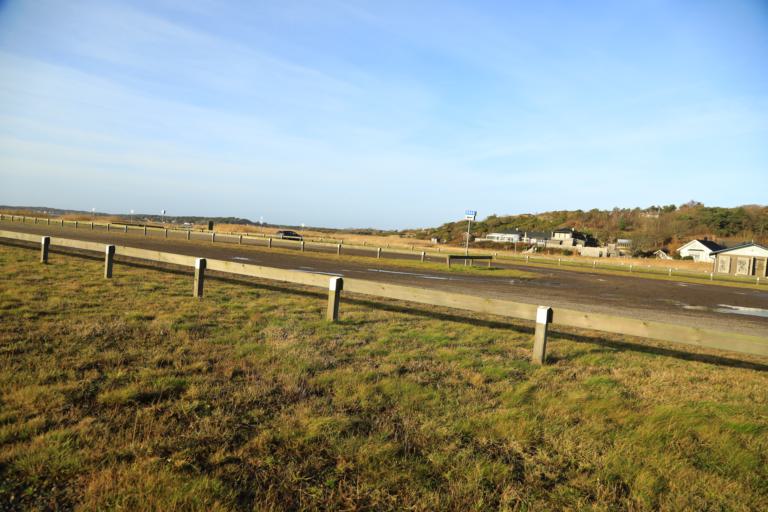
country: SE
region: Halland
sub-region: Varbergs Kommun
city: Varberg
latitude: 57.1837
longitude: 12.2155
